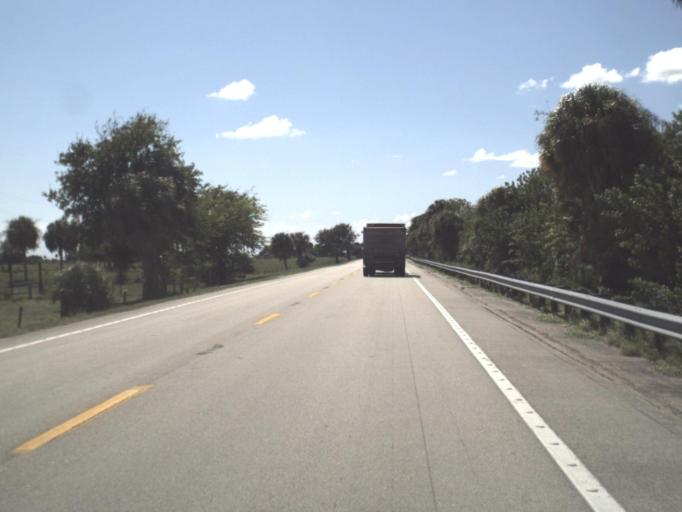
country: US
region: Florida
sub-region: Glades County
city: Buckhead Ridge
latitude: 27.0961
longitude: -80.9556
